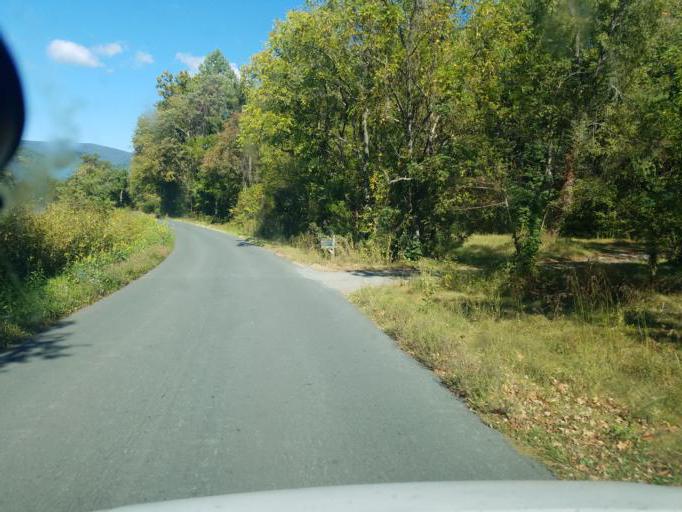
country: US
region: Virginia
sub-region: Greene County
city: Stanardsville
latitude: 38.3526
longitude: -78.4116
